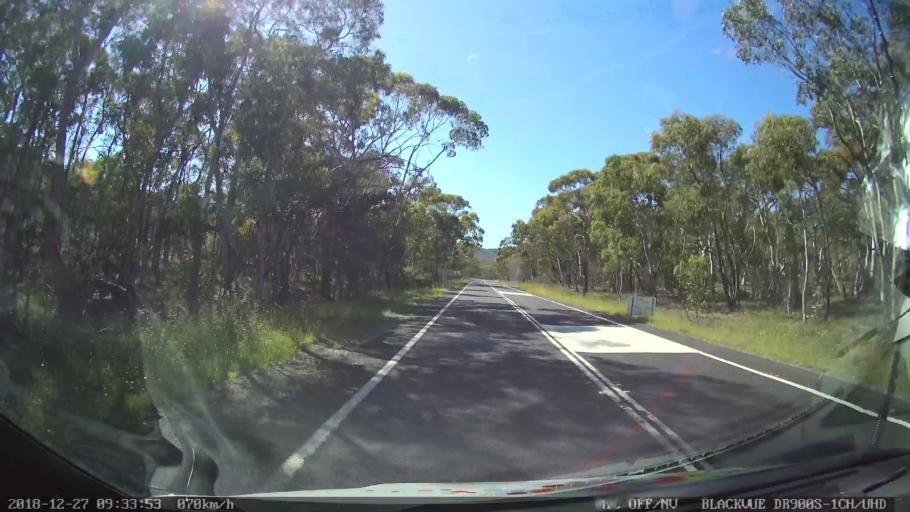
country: AU
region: New South Wales
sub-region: Lithgow
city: Portland
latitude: -33.2203
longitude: 150.0241
